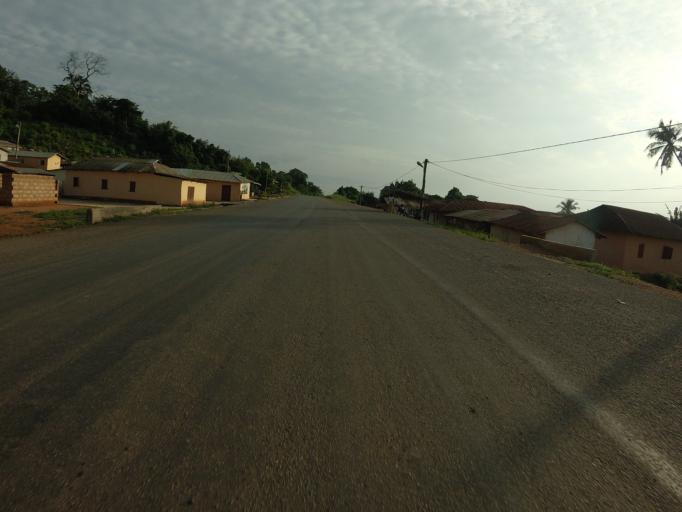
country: GH
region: Volta
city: Kpandu
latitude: 6.9128
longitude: 0.4497
